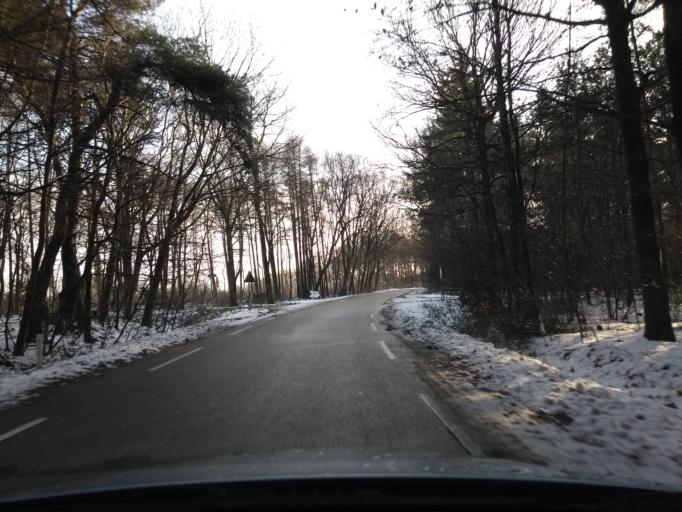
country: NL
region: Gelderland
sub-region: Gemeente Bronckhorst
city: Zelhem
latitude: 52.0525
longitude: 6.4059
